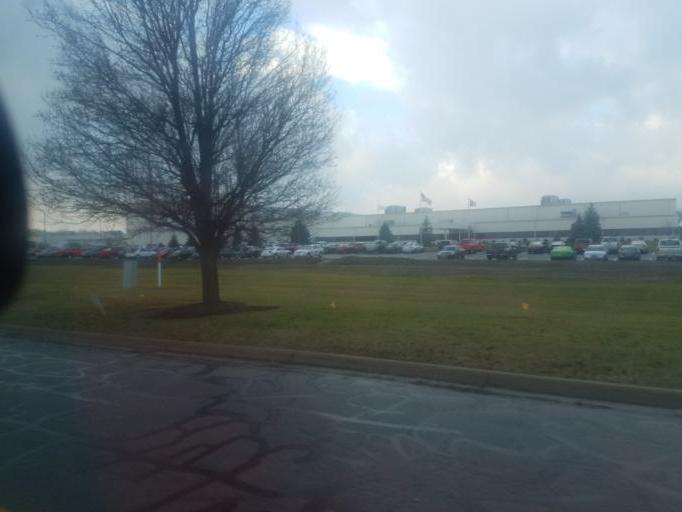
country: US
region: Ohio
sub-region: Marion County
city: Marion
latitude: 40.6114
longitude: -83.1411
